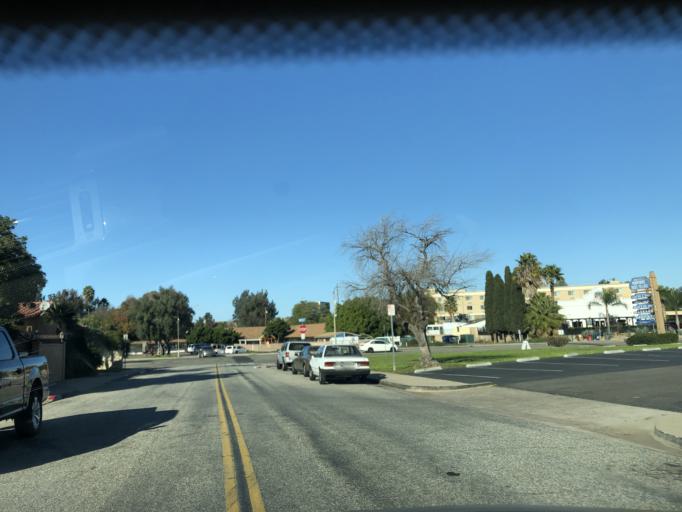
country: US
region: California
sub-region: San Diego County
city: Chula Vista
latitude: 32.6473
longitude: -117.0655
